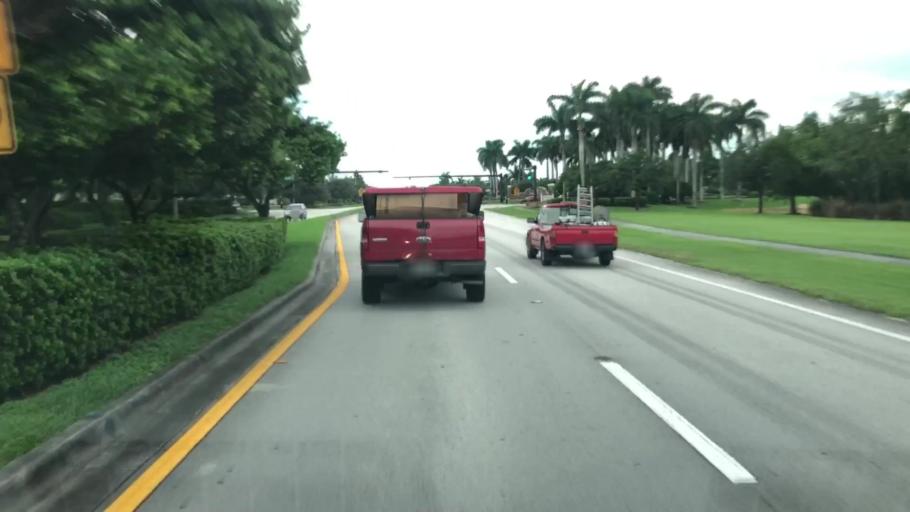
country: US
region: Florida
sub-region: Broward County
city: Coral Springs
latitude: 26.3102
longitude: -80.2789
